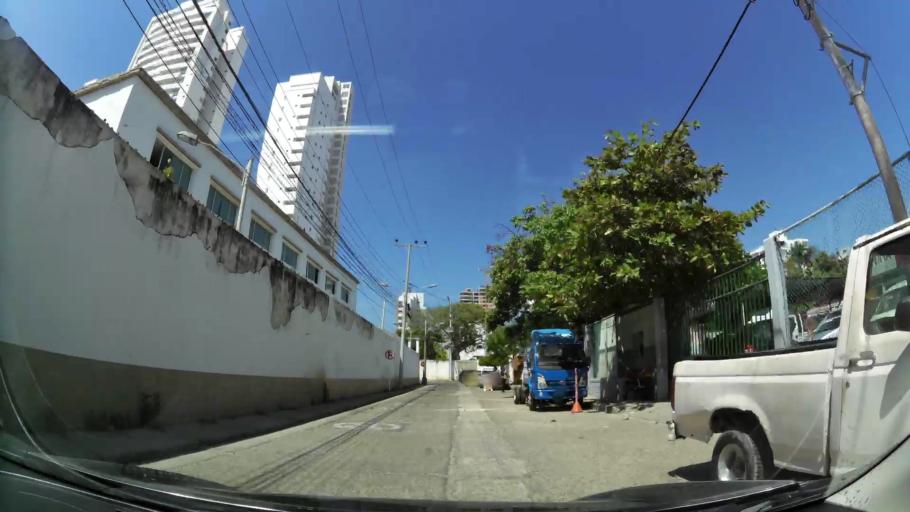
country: CO
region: Bolivar
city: Cartagena
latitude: 10.4092
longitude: -75.5359
